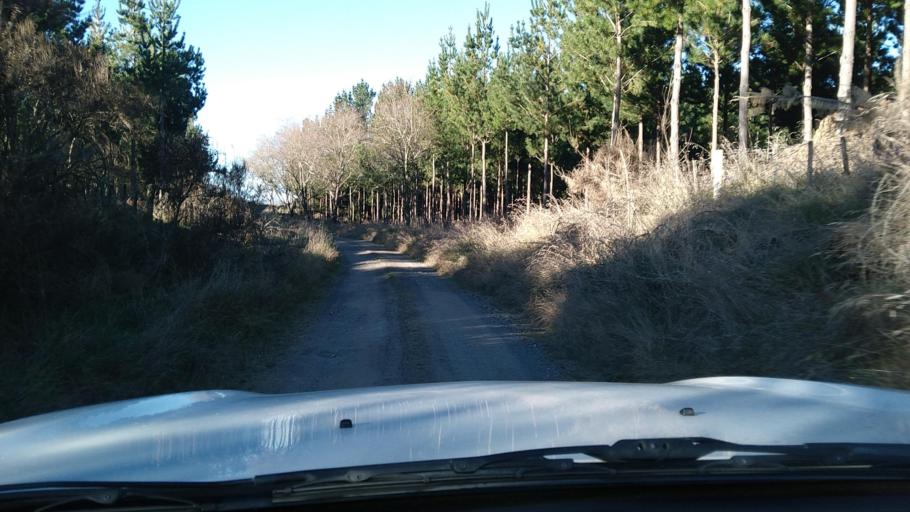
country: NZ
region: Waikato
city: Turangi
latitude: -38.6421
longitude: 175.7017
